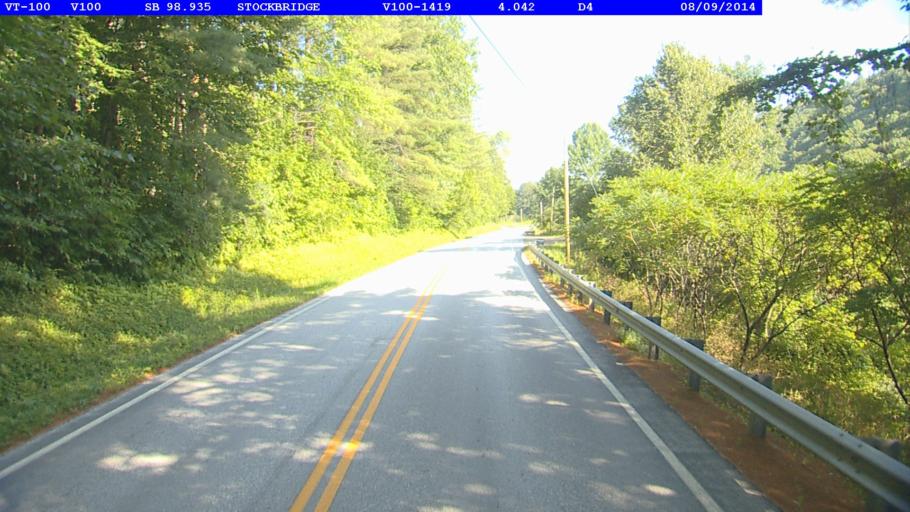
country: US
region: Vermont
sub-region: Orange County
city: Randolph
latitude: 43.7955
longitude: -72.7672
